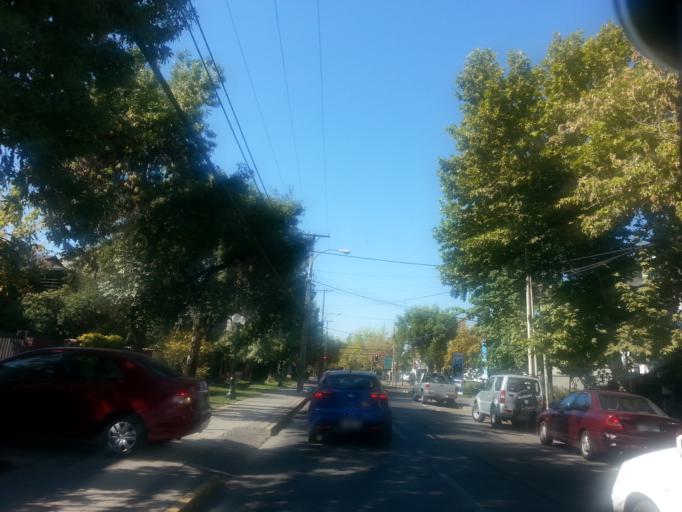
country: CL
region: Santiago Metropolitan
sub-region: Provincia de Santiago
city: Villa Presidente Frei, Nunoa, Santiago, Chile
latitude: -33.4352
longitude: -70.5956
